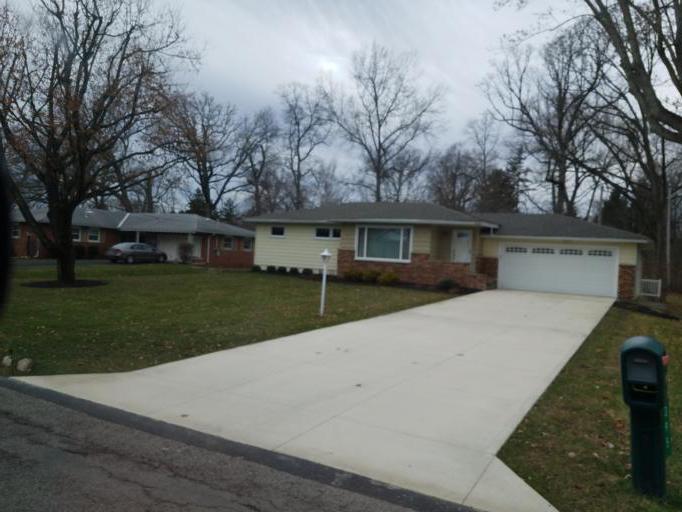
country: US
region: Ohio
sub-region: Marion County
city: Marion
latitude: 40.5774
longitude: -83.0971
